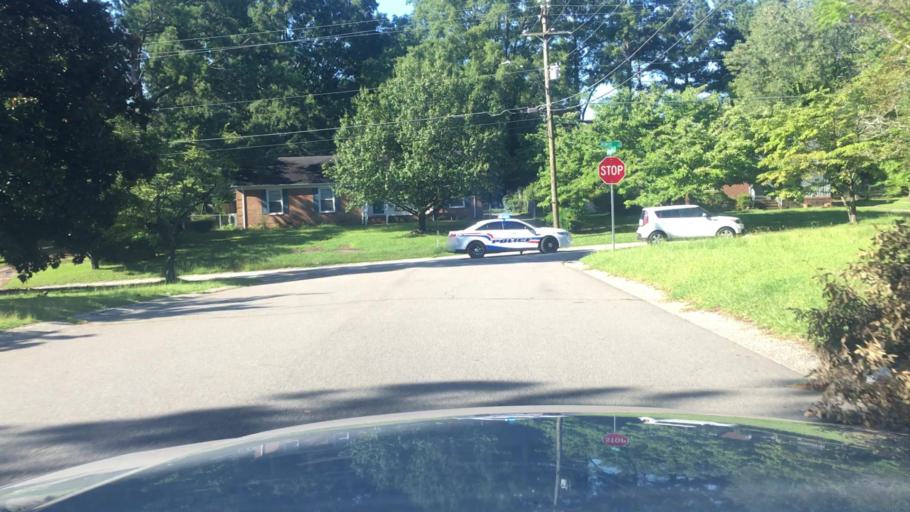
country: US
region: North Carolina
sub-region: Cumberland County
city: Fayetteville
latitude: 35.1359
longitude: -78.8898
